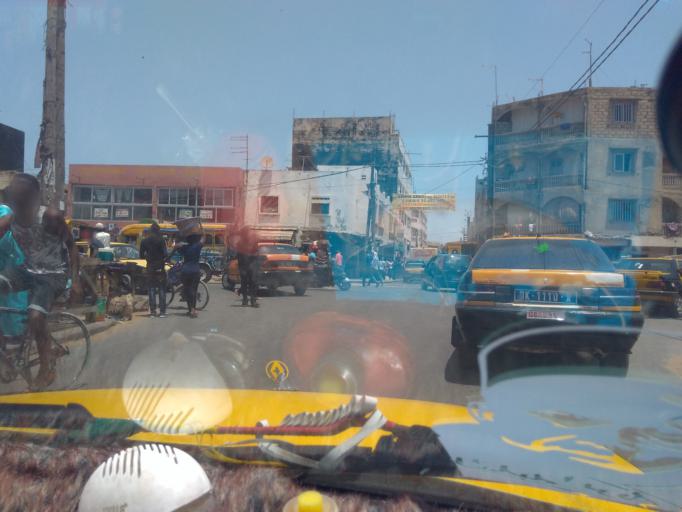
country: SN
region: Dakar
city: Grand Dakar
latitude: 14.7398
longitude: -17.4467
